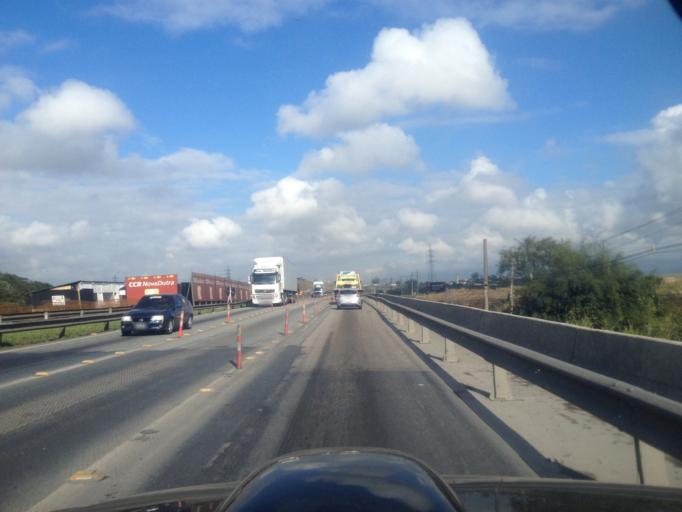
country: BR
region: Rio de Janeiro
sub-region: Resende
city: Resende
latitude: -22.4532
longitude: -44.3681
